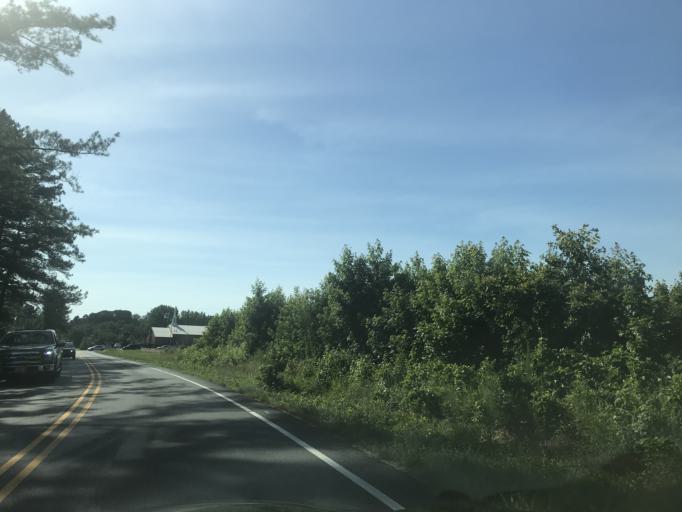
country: US
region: North Carolina
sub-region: Wake County
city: Garner
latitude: 35.6607
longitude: -78.5452
